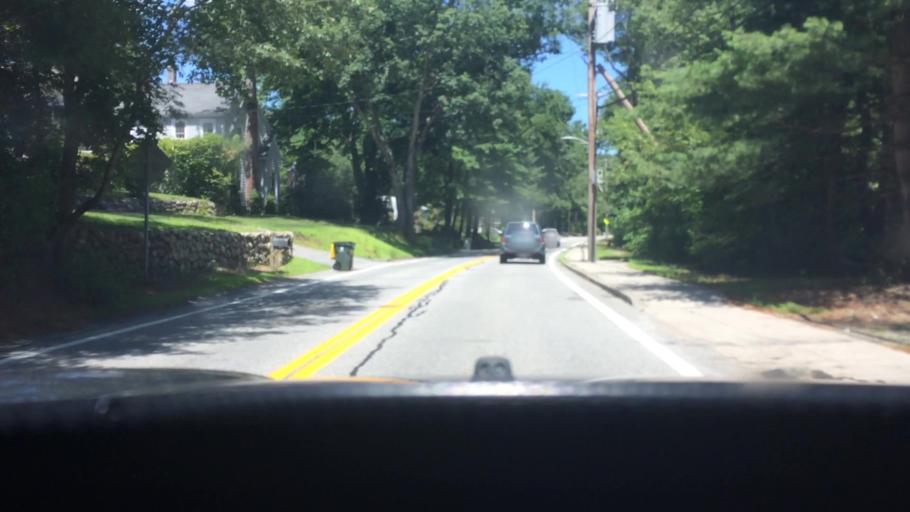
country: US
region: Rhode Island
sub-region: Providence County
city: Harrisville
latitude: 41.9675
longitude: -71.6656
